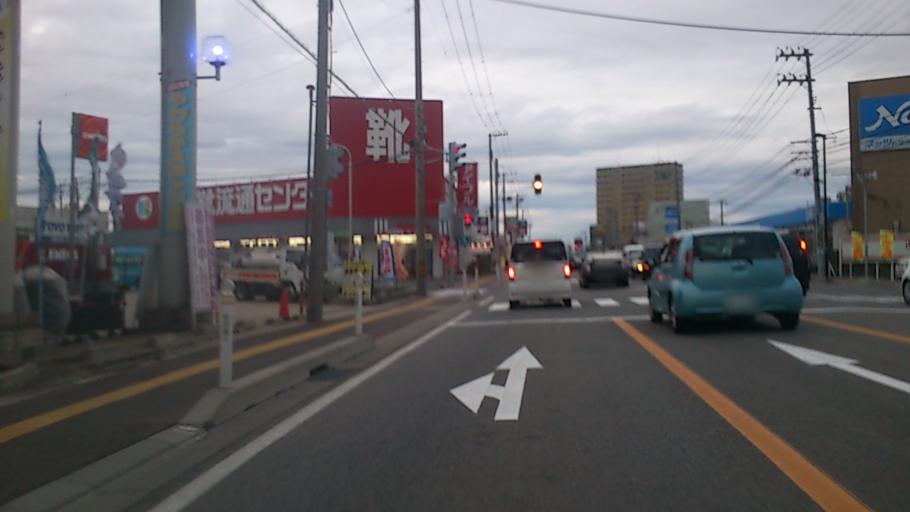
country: JP
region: Akita
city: Akita Shi
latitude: 39.7391
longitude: 140.0960
